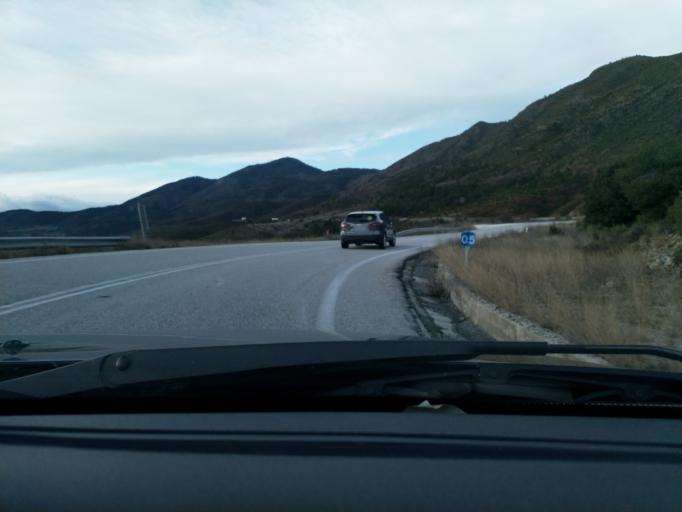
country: GR
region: Thessaly
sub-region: Trikala
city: Kastraki
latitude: 39.7723
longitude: 21.4513
